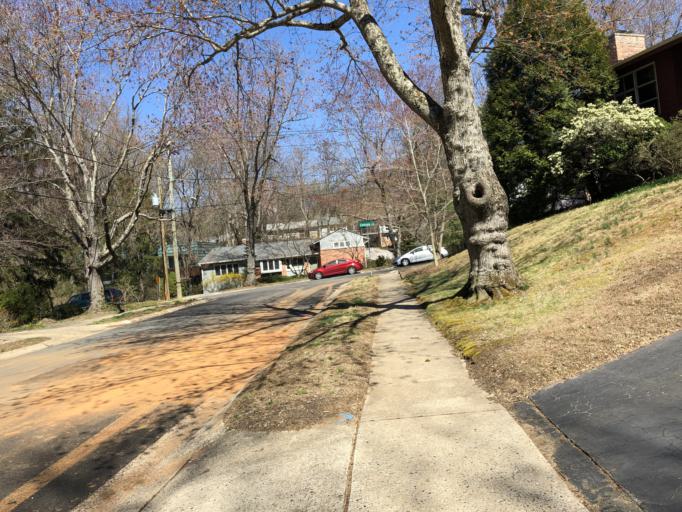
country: US
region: Maryland
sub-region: Montgomery County
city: Cabin John
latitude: 38.9745
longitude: -77.1417
